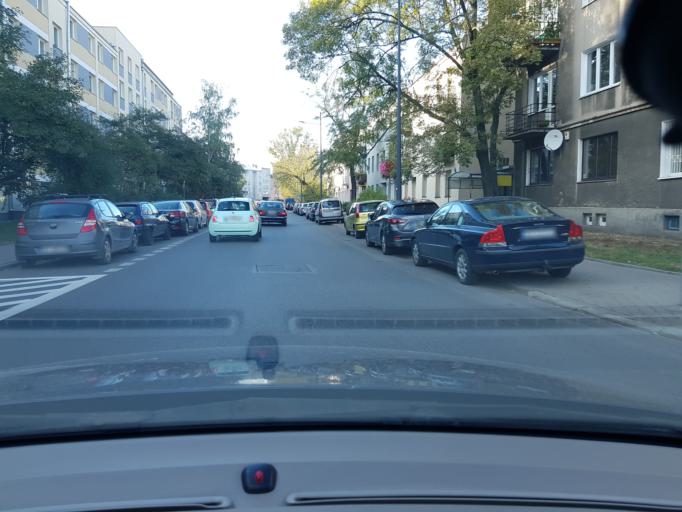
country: PL
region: Masovian Voivodeship
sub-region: Warszawa
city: Praga Poludnie
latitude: 52.2438
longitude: 21.0771
